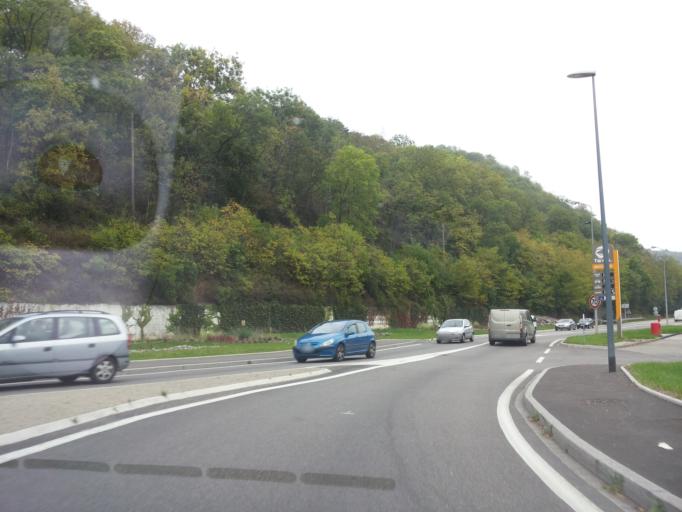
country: FR
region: Alsace
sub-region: Departement du Bas-Rhin
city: Wasselonne
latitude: 48.6349
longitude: 7.4598
